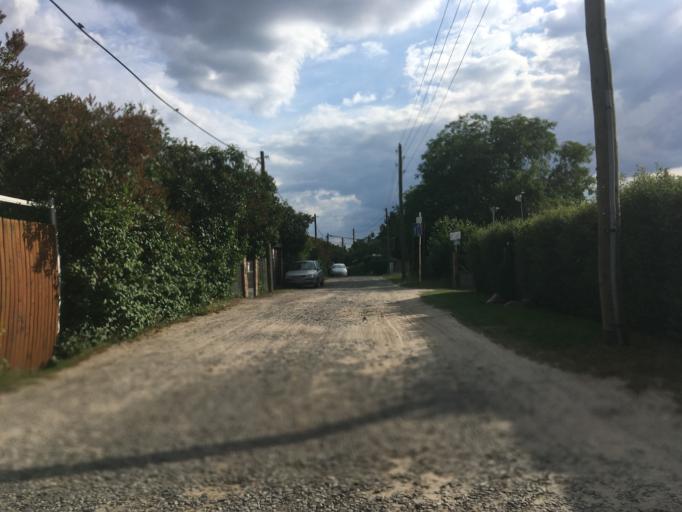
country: DE
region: Berlin
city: Johannisthal
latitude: 52.4445
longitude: 13.4900
